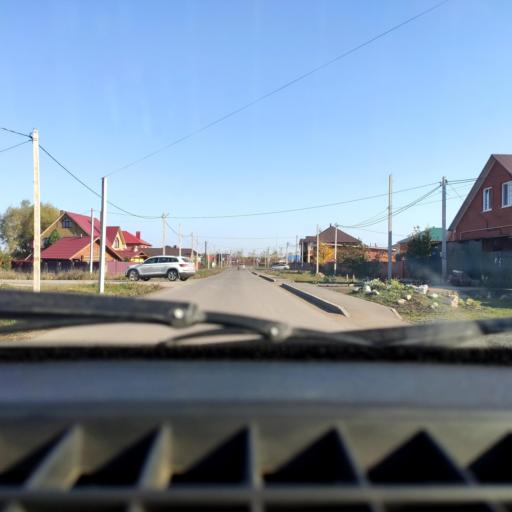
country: RU
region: Bashkortostan
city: Ufa
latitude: 54.6232
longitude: 55.9032
